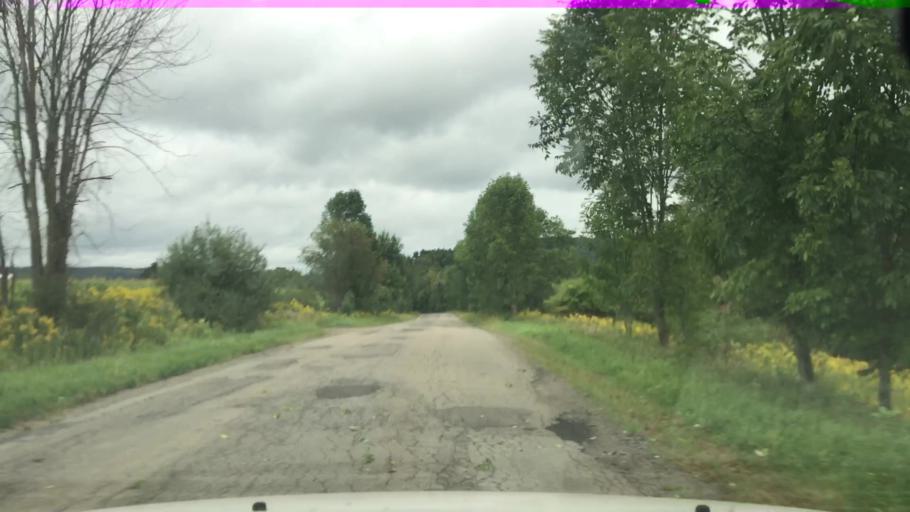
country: US
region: New York
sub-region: Cattaraugus County
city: Little Valley
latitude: 42.3238
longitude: -78.7245
